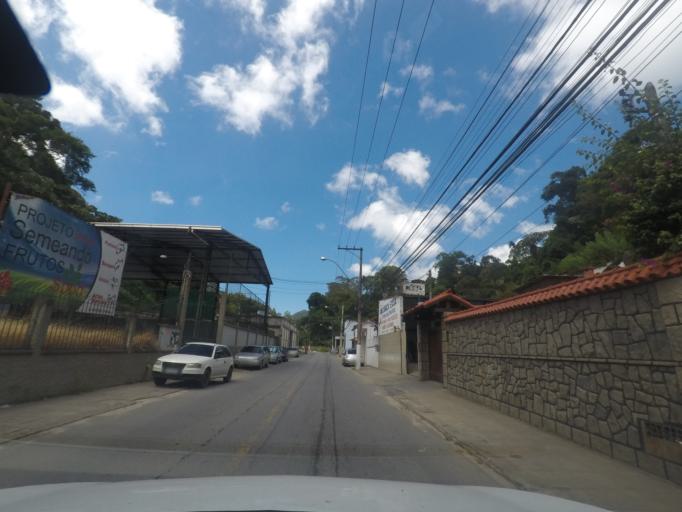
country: BR
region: Rio de Janeiro
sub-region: Teresopolis
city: Teresopolis
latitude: -22.4070
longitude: -42.9788
